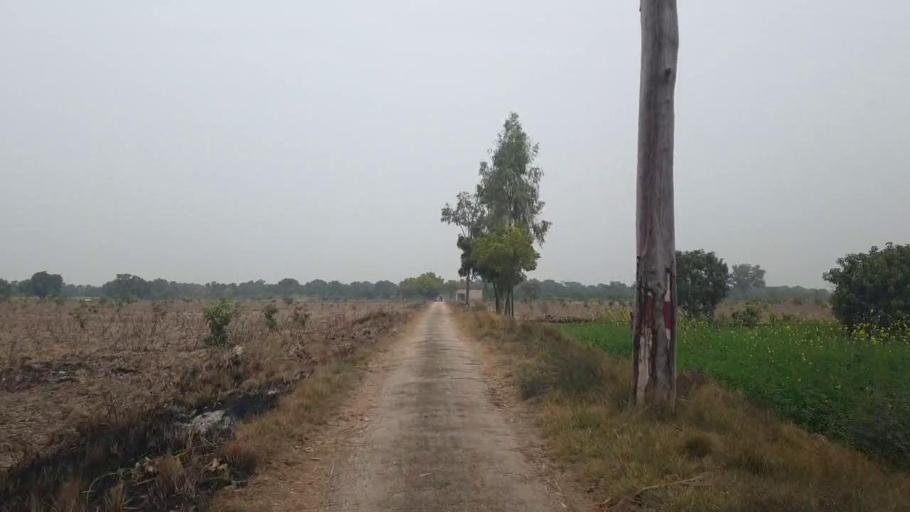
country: PK
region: Sindh
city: Tando Adam
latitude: 25.8153
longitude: 68.6695
